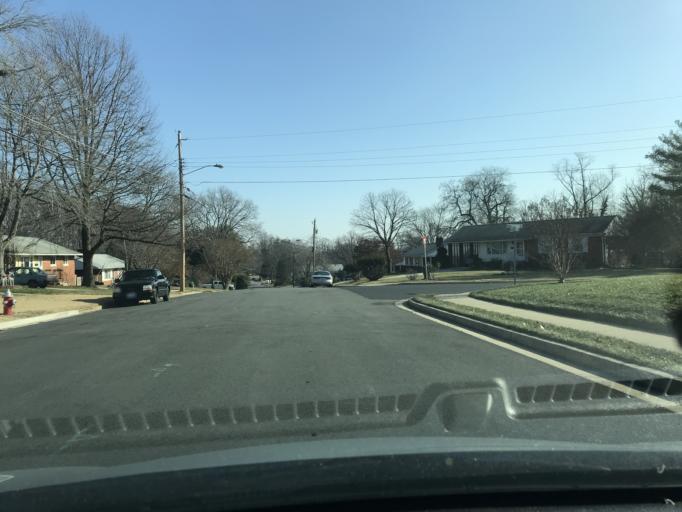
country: US
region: Virginia
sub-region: City of Fairfax
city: Fairfax
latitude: 38.8579
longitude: -77.3246
